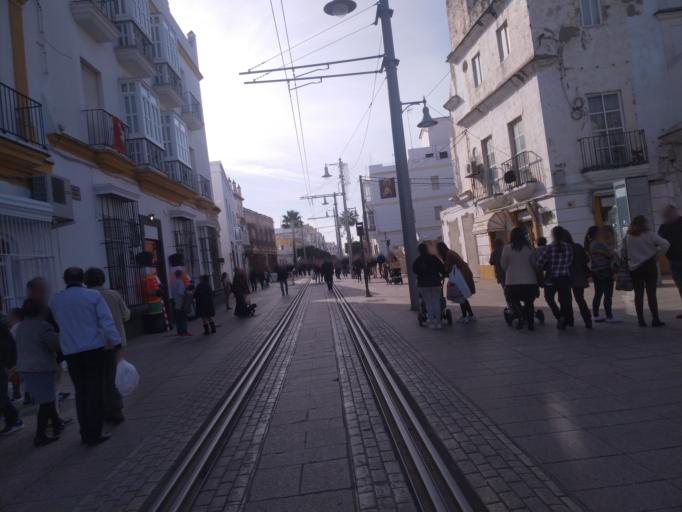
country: ES
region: Andalusia
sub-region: Provincia de Cadiz
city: San Fernando
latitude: 36.4627
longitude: -6.1998
